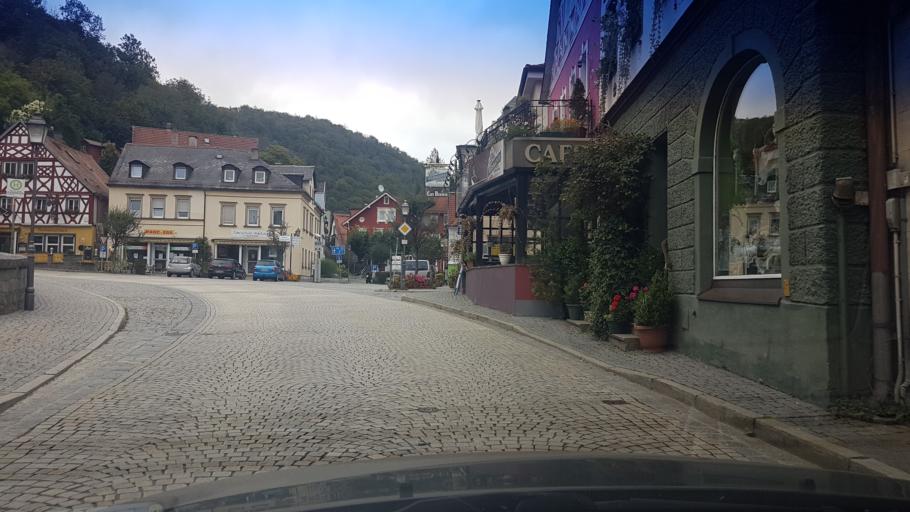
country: DE
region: Bavaria
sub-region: Upper Franconia
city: Bad Berneck im Fichtelgebirge
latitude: 50.0491
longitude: 11.6755
